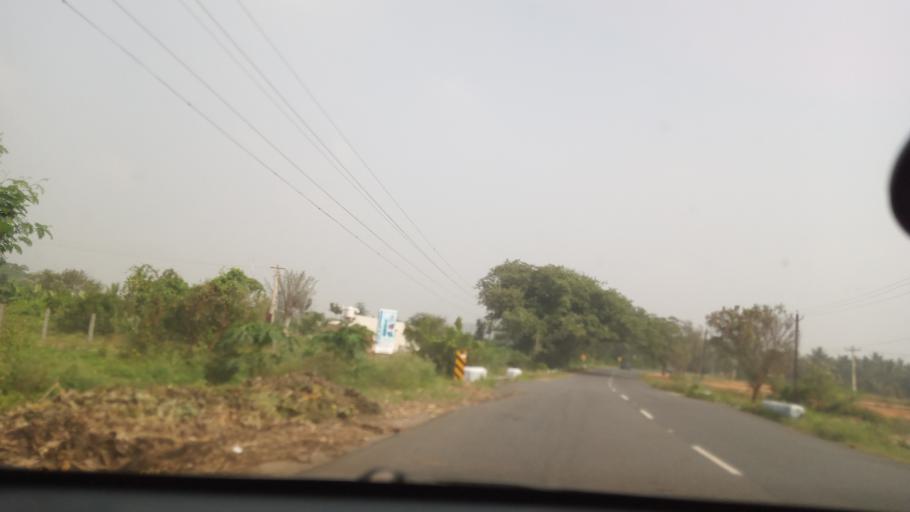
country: IN
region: Tamil Nadu
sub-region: Erode
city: Punjai Puliyampatti
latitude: 11.3236
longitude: 77.1482
